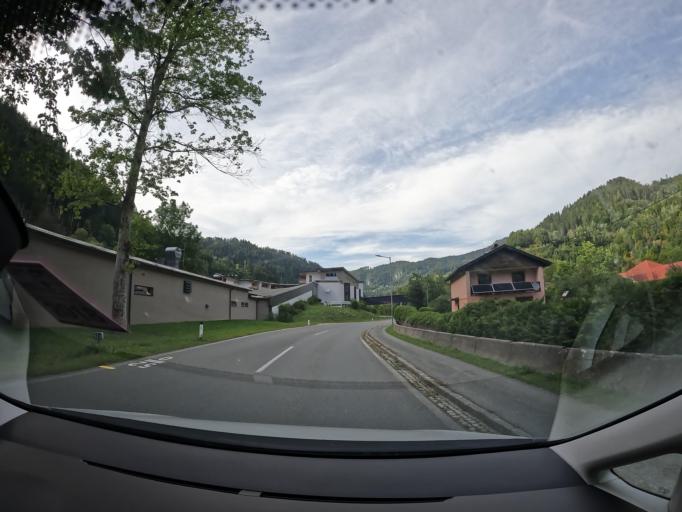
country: AT
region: Carinthia
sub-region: Politischer Bezirk Volkermarkt
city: Bad Eisenkappel
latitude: 46.4769
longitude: 14.5925
